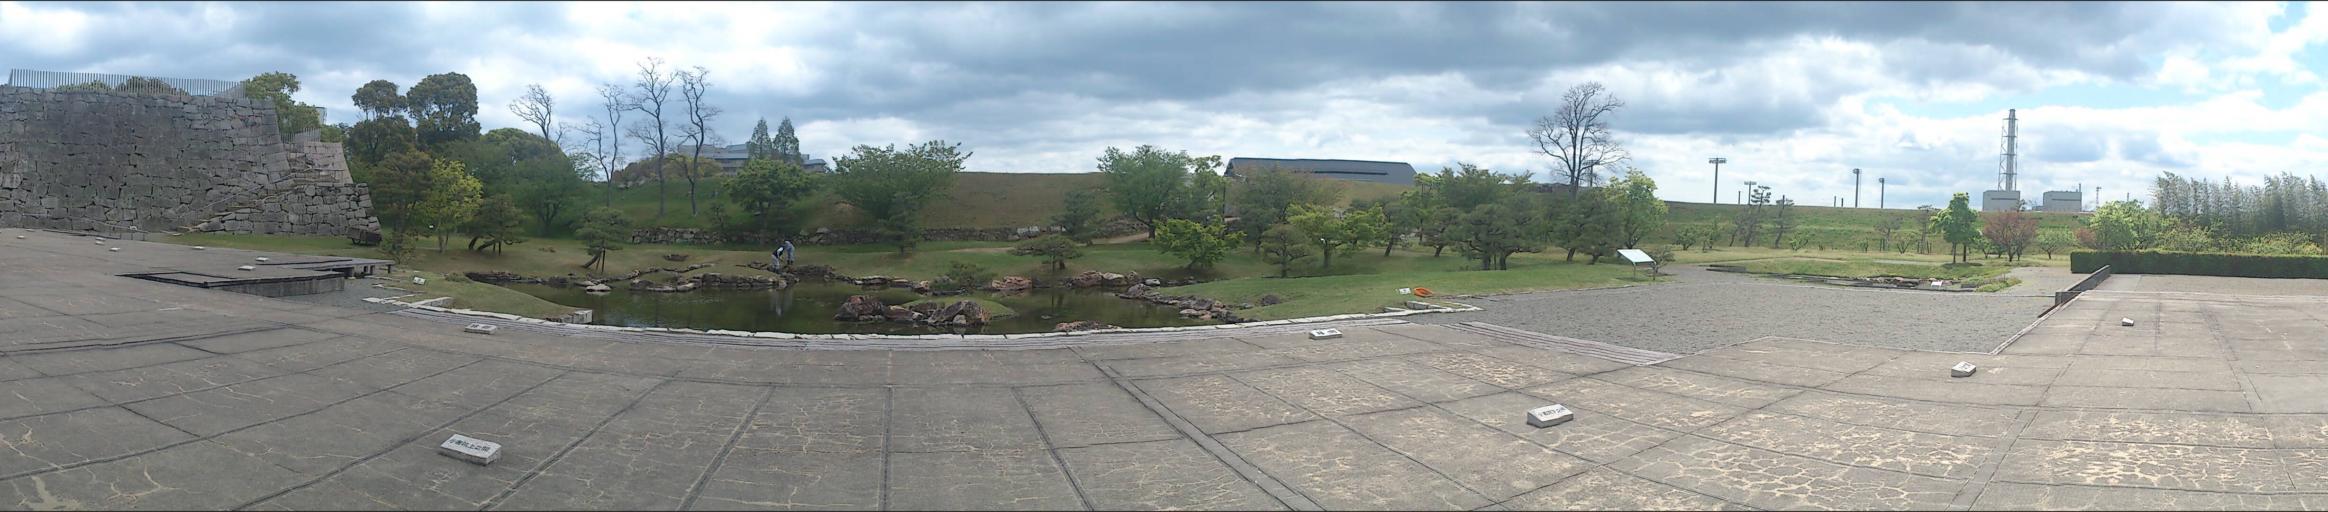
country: JP
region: Hyogo
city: Kariya
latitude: 34.7484
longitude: 134.3904
